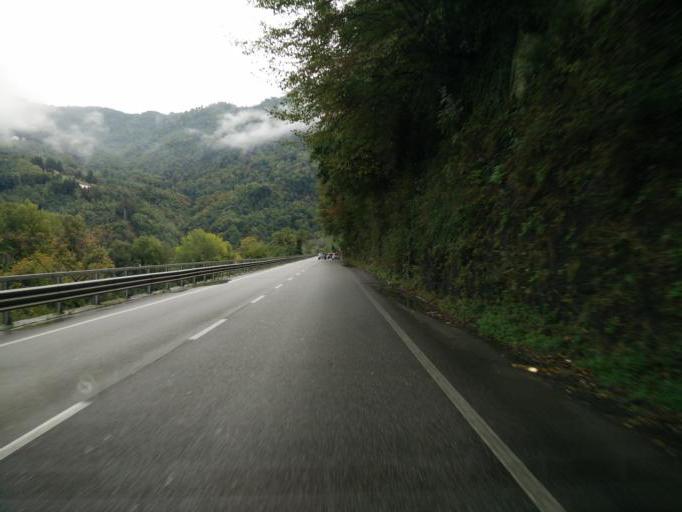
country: IT
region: Tuscany
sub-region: Provincia di Lucca
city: Valdottavo
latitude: 43.9345
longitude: 10.5027
